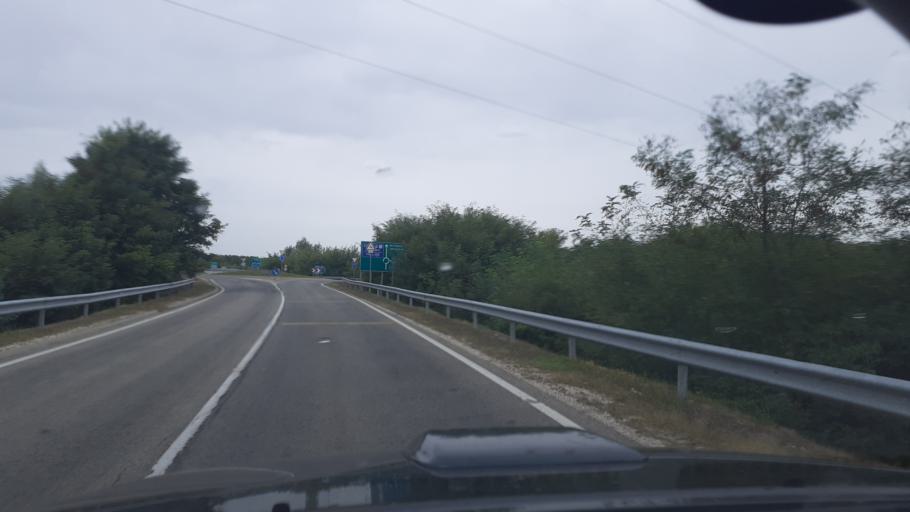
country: HU
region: Fejer
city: Baracs
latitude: 46.8547
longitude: 18.8779
